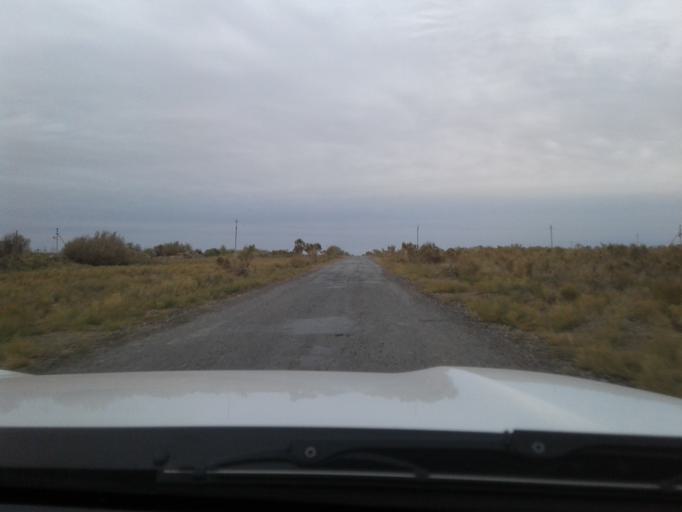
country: TM
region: Mary
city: Mary
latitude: 38.1389
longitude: 61.7872
